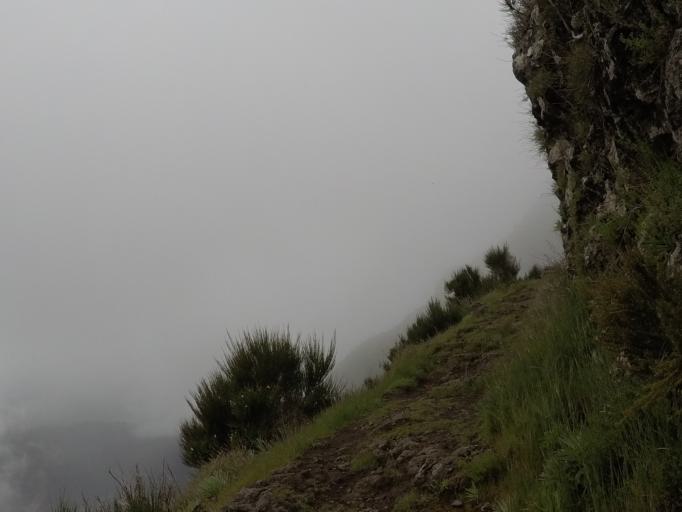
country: PT
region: Madeira
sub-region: Camara de Lobos
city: Curral das Freiras
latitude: 32.7161
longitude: -16.9895
